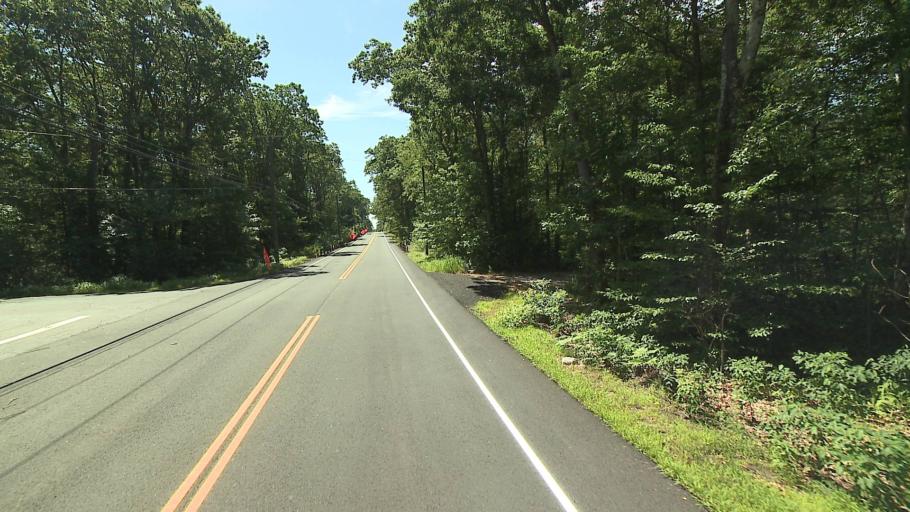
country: US
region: Connecticut
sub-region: Litchfield County
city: New Hartford Center
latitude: 41.9527
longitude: -72.9153
